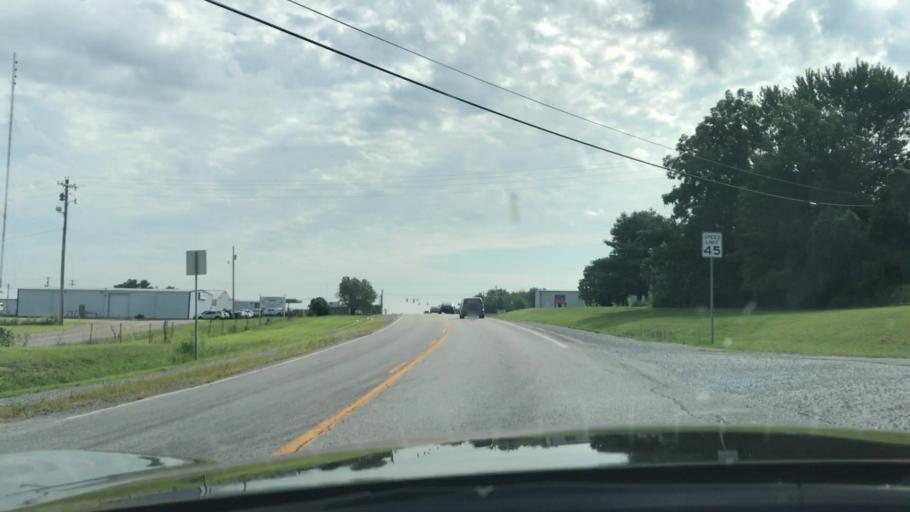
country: US
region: Kentucky
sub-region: Taylor County
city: Campbellsville
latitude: 37.3325
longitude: -85.3782
